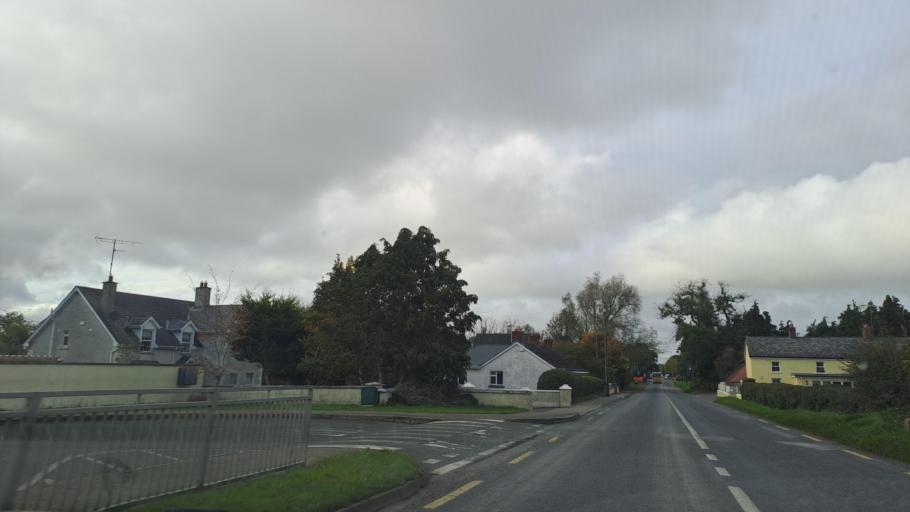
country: IE
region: Leinster
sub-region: An Mhi
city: Navan
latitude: 53.7320
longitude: -6.7094
